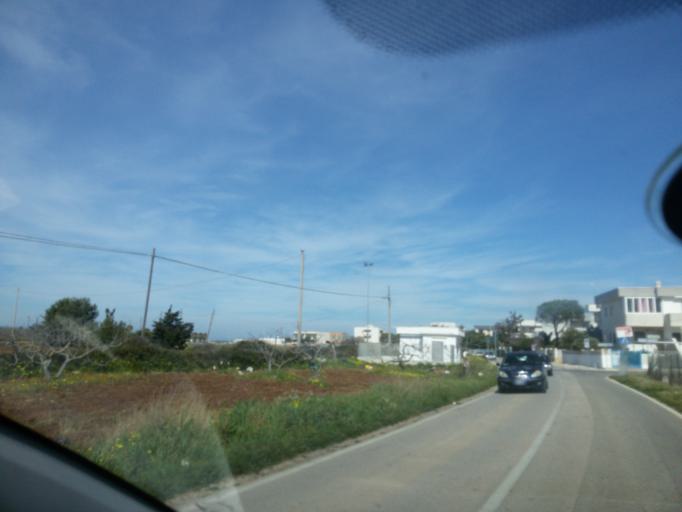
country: IT
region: Apulia
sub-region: Provincia di Brindisi
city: Pezze di Greco
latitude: 40.8406
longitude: 17.4643
